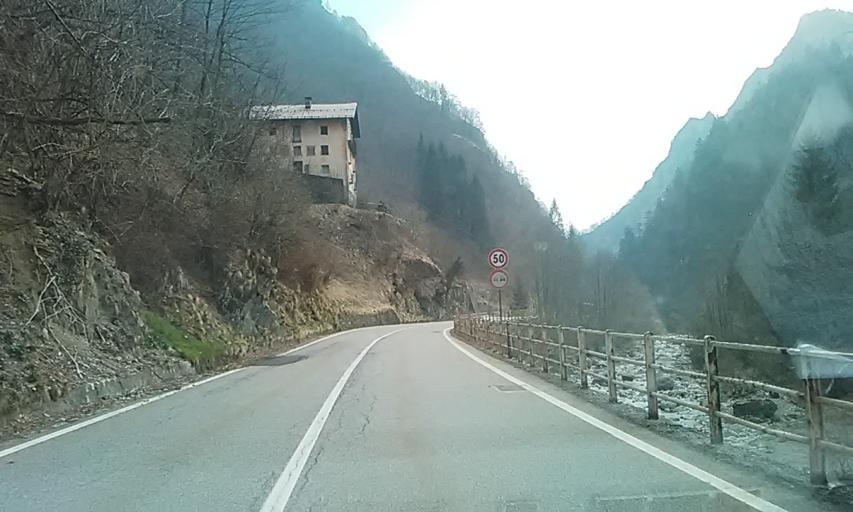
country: IT
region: Piedmont
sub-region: Provincia di Vercelli
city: Fobello
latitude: 45.8881
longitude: 8.1622
